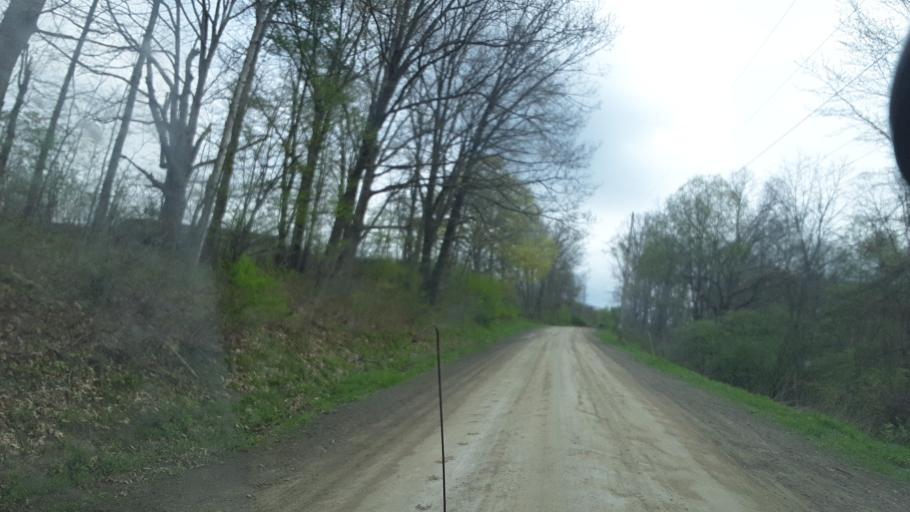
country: US
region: New York
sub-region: Steuben County
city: Addison
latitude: 42.0983
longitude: -77.3342
